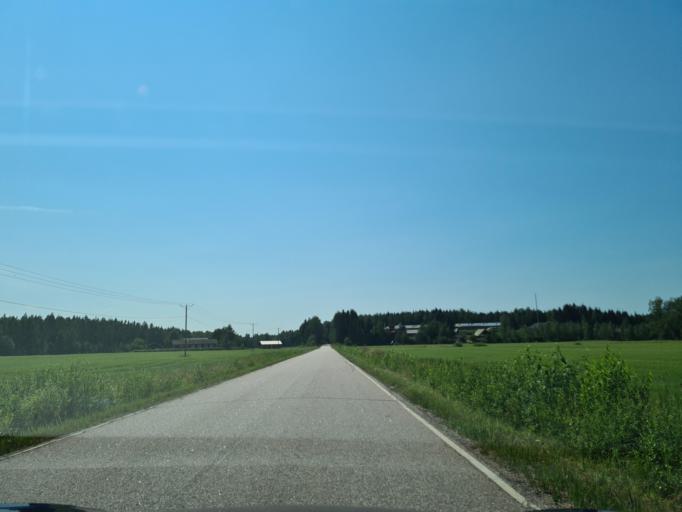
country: FI
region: Varsinais-Suomi
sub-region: Loimaa
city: Aura
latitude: 60.6057
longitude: 22.6113
